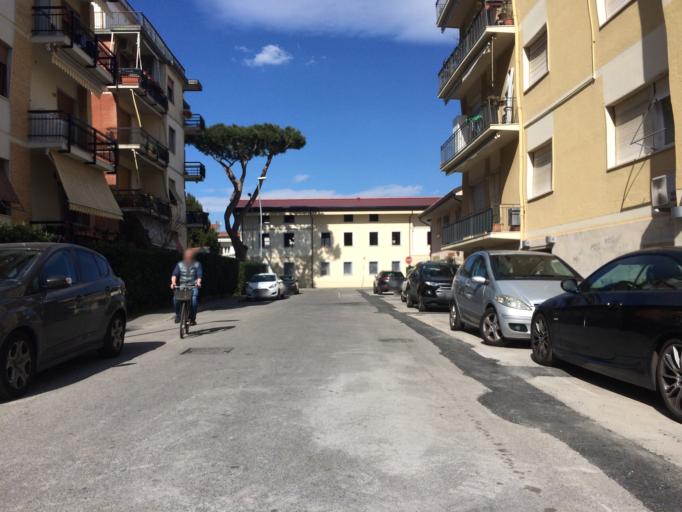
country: IT
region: Tuscany
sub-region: Provincia di Massa-Carrara
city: Marina di Carrara
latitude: 44.0432
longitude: 10.0357
